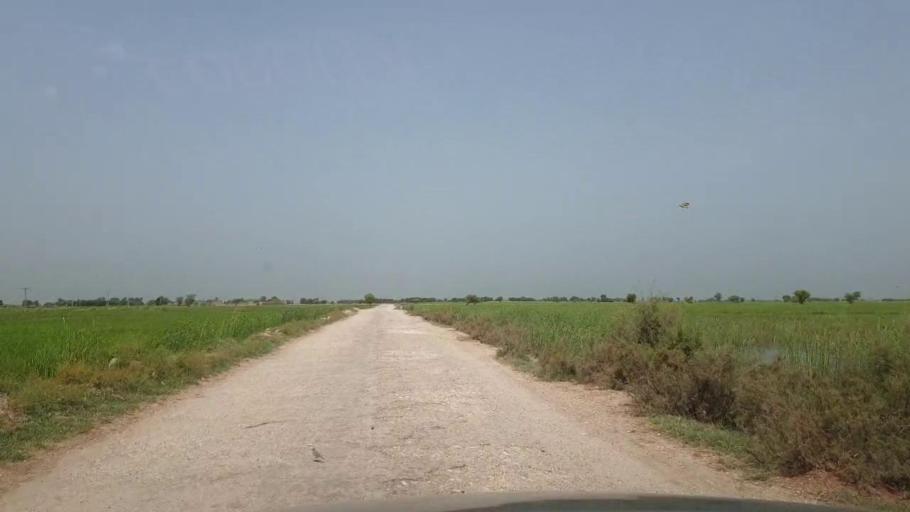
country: PK
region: Sindh
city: Garhi Yasin
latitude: 27.8593
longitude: 68.4088
